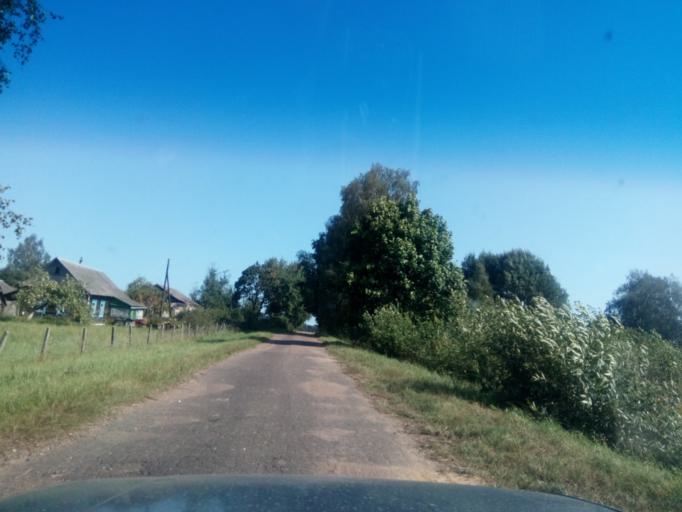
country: BY
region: Vitebsk
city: Dzisna
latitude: 55.6422
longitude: 28.2411
